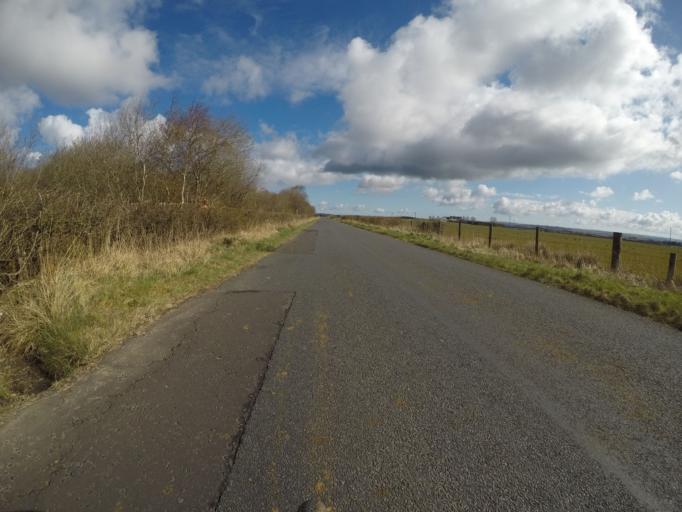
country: GB
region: Scotland
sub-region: North Ayrshire
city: Kilwinning
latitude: 55.6809
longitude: -4.6525
